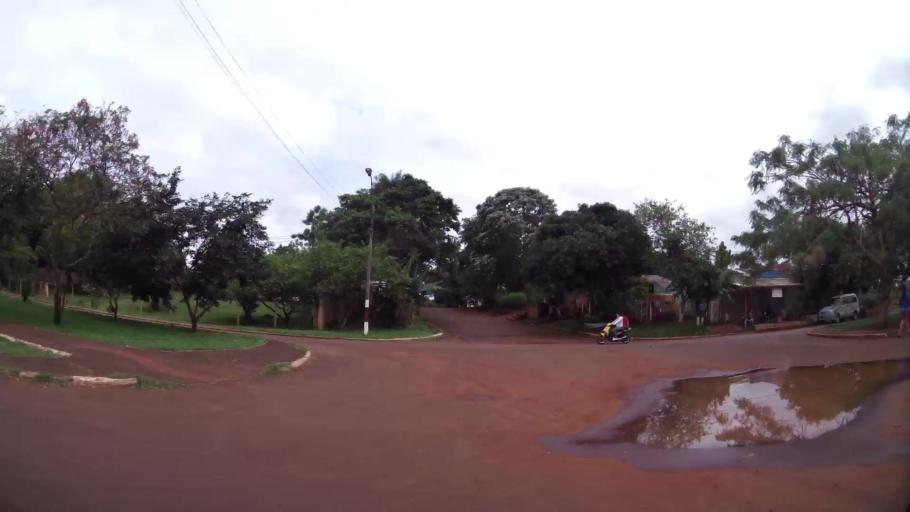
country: PY
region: Alto Parana
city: Ciudad del Este
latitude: -25.4052
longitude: -54.6348
